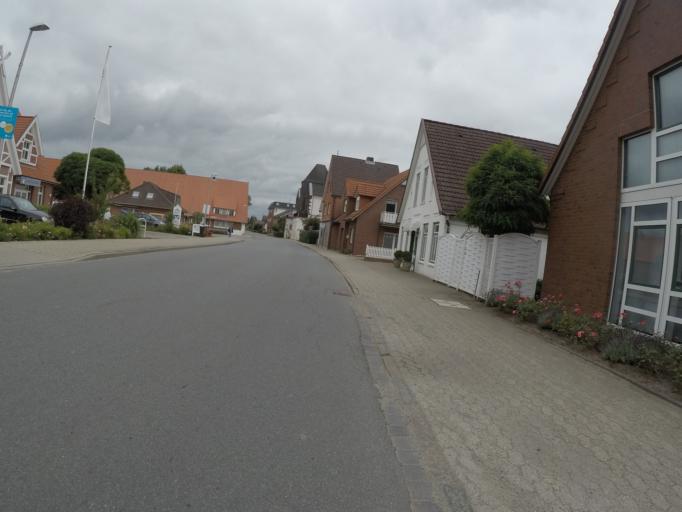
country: DE
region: Lower Saxony
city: Steinkirchen
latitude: 53.5612
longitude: 9.6092
